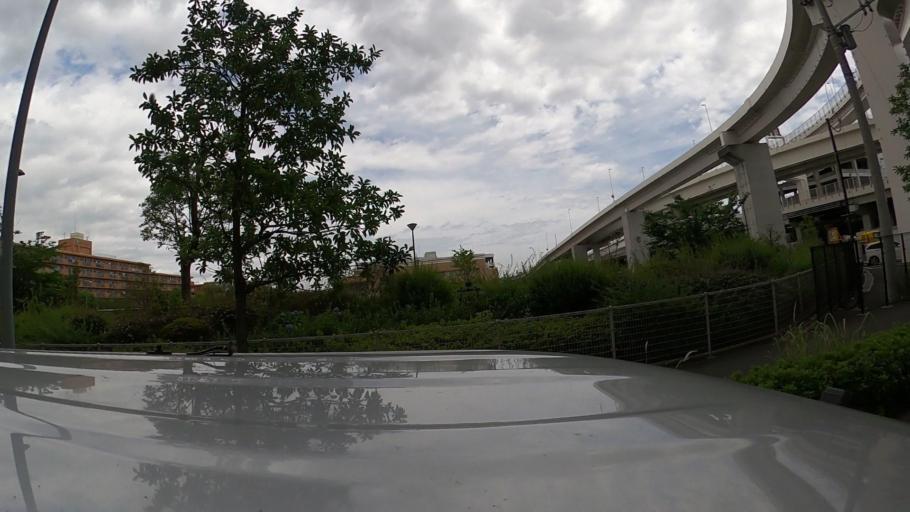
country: JP
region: Kanagawa
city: Yokohama
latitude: 35.4921
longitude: 139.6705
